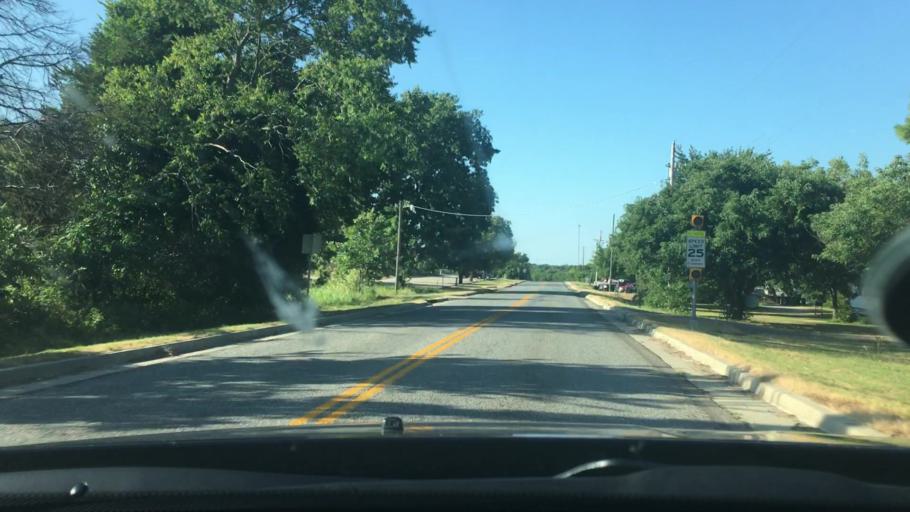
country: US
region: Oklahoma
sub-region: Murray County
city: Sulphur
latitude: 34.4000
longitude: -96.8271
